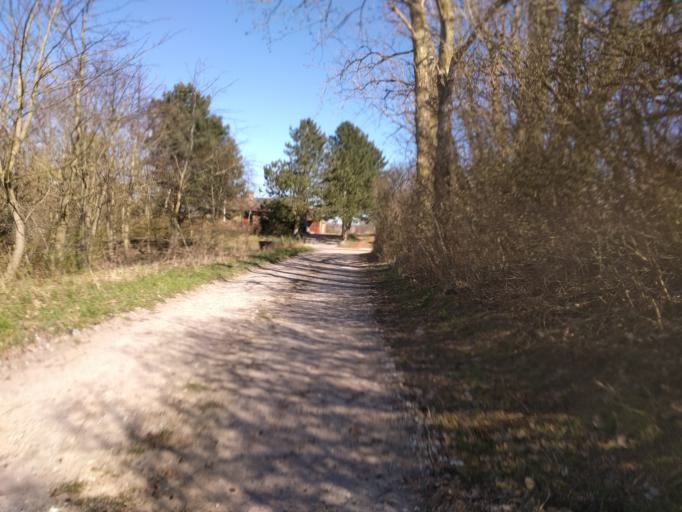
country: DK
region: South Denmark
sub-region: Kerteminde Kommune
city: Langeskov
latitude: 55.3742
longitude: 10.5837
